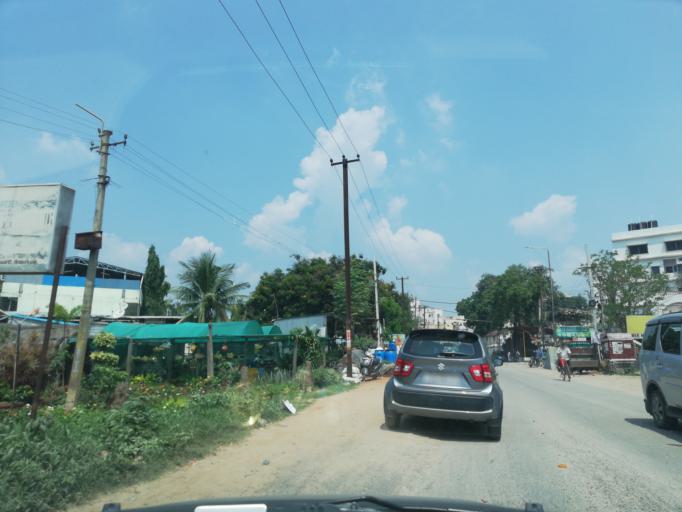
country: IN
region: Telangana
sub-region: Medak
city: Serilingampalle
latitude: 17.4889
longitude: 78.3198
